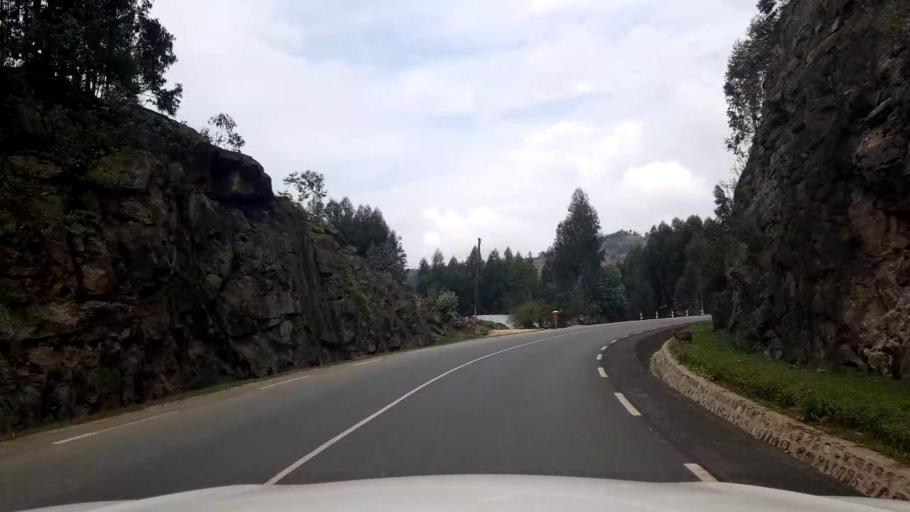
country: RW
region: Northern Province
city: Musanze
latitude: -1.6638
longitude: 29.5159
